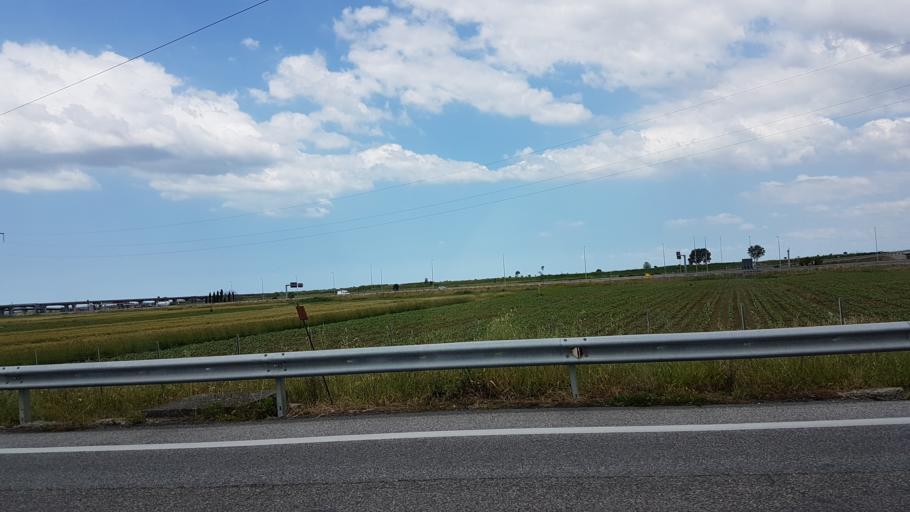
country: IT
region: Tuscany
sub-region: Provincia di Livorno
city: Vicarello
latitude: 43.6168
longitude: 10.4482
